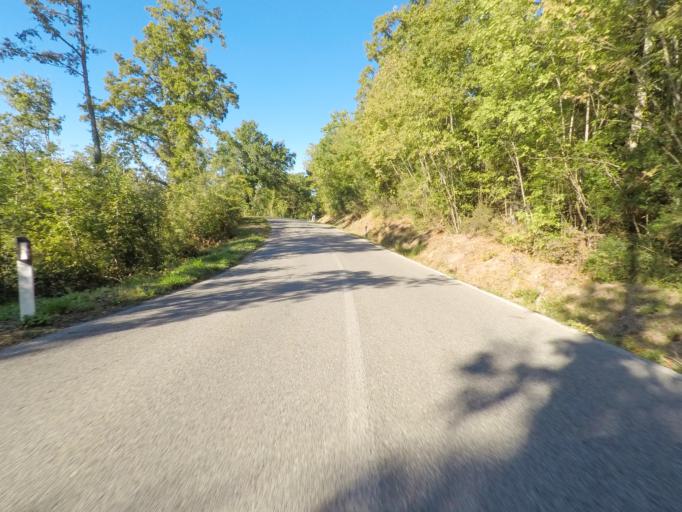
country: IT
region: Tuscany
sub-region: Provincia di Siena
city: Belverde
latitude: 43.3853
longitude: 11.3445
